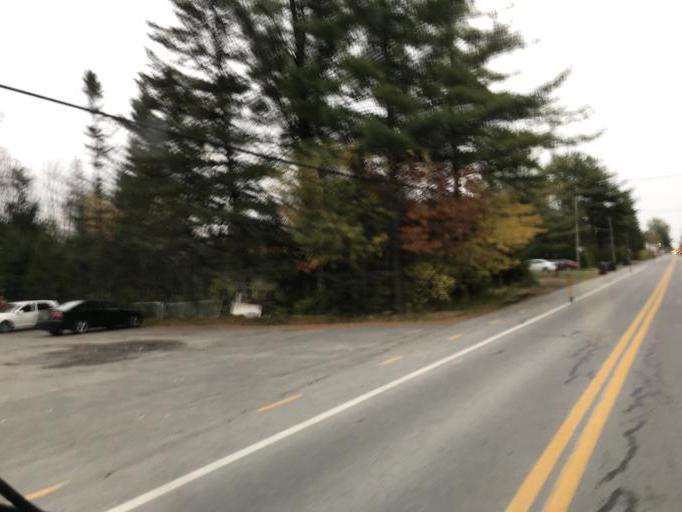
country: CA
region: Quebec
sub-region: Lanaudiere
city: Lorraine
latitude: 45.6860
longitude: -73.7919
